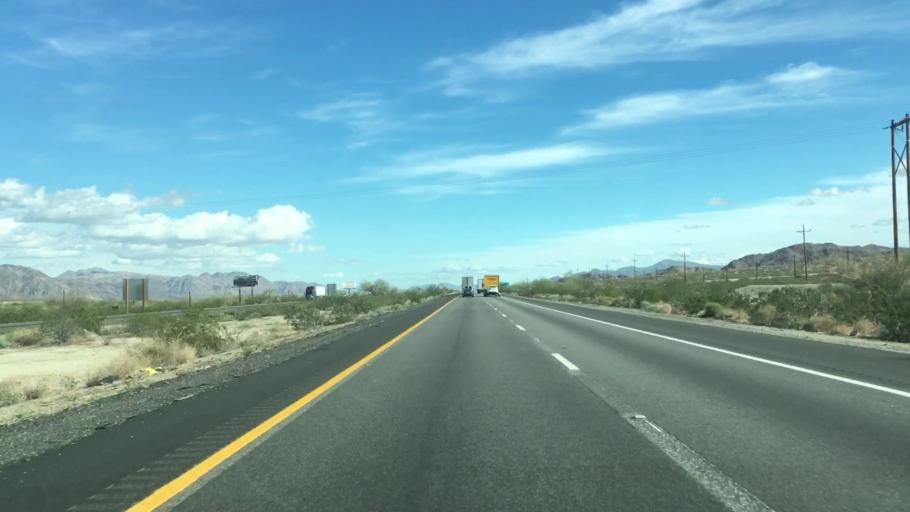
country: US
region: California
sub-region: Riverside County
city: Mecca
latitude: 33.6609
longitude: -115.7150
